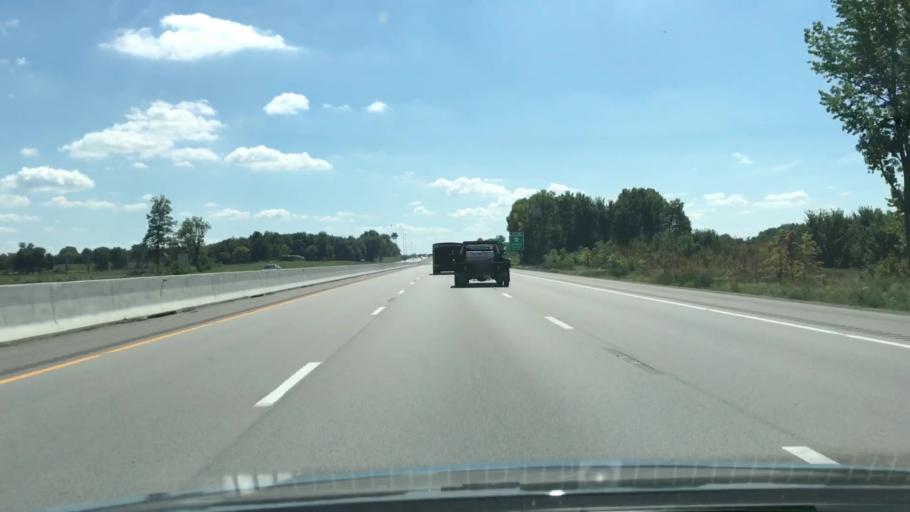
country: US
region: Kentucky
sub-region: Larue County
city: Hodgenville
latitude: 37.5353
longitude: -85.8825
